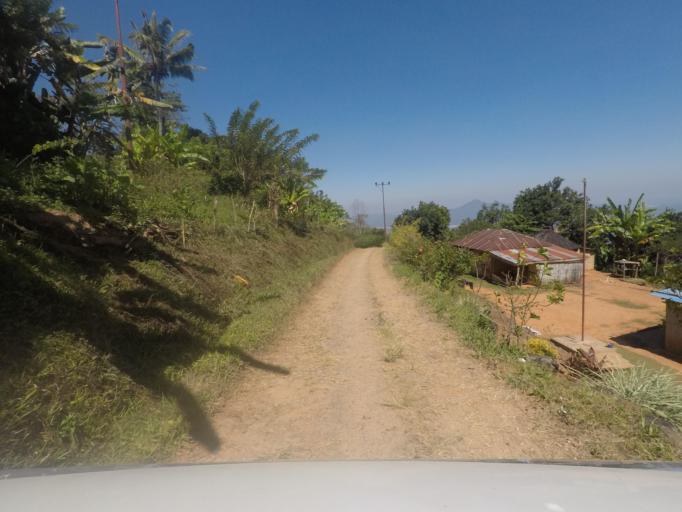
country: TL
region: Ermera
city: Gleno
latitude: -8.7190
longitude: 125.3172
